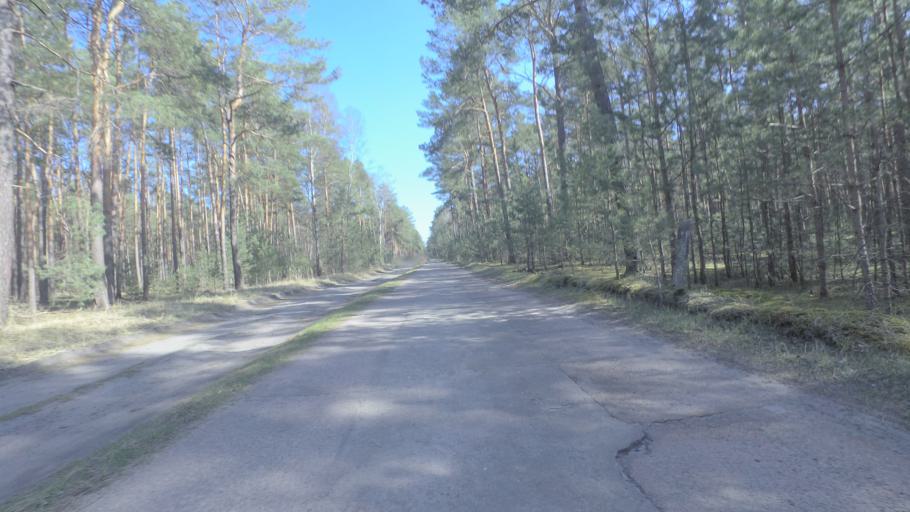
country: DE
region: Brandenburg
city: Halbe
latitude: 52.1737
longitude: 13.7419
